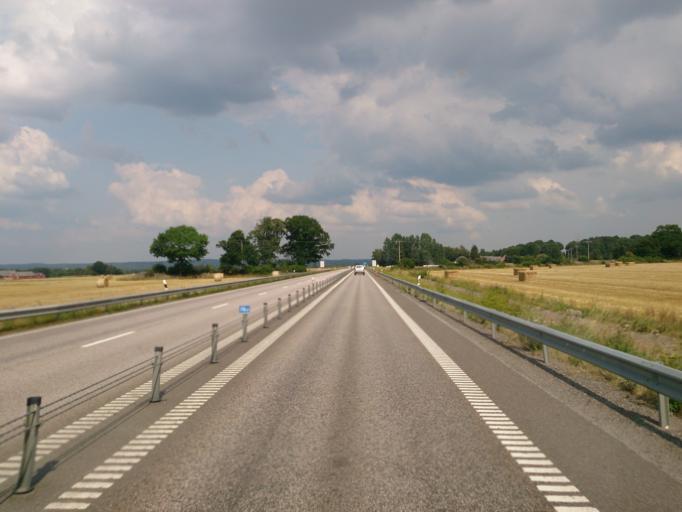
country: SE
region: Skane
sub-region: Hoors Kommun
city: Satofta
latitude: 55.8400
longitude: 13.5750
